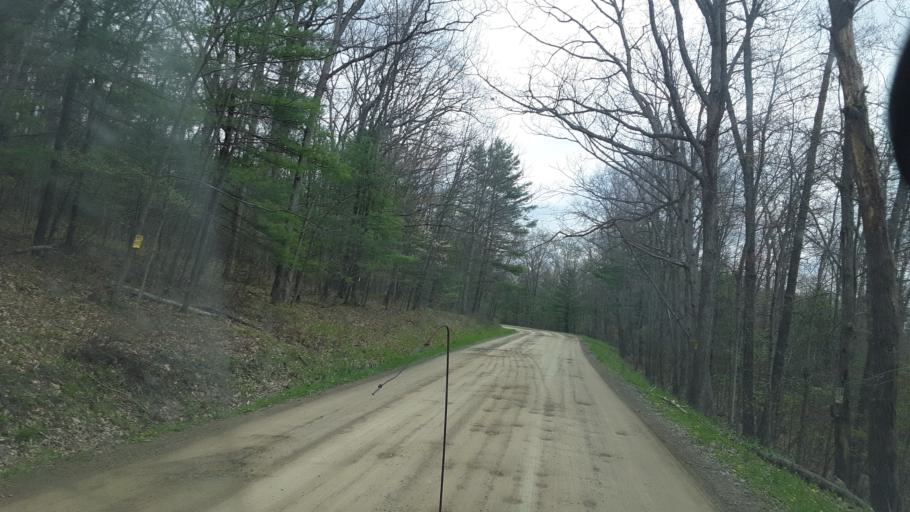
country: US
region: New York
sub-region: Steuben County
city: Addison
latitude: 42.0938
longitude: -77.3217
